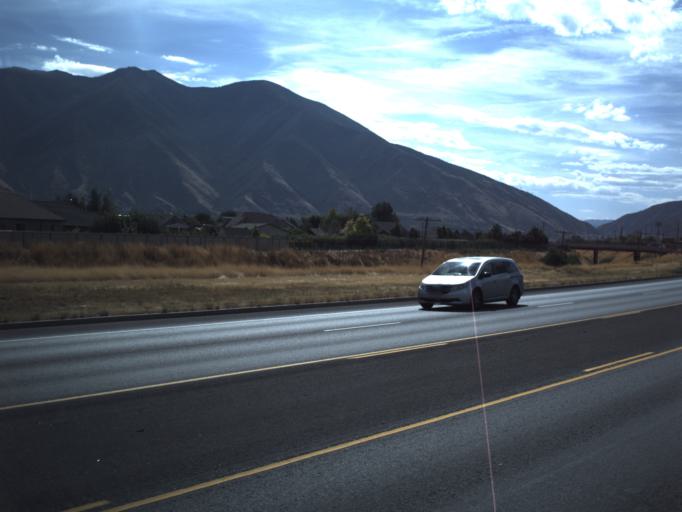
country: US
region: Utah
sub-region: Utah County
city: Spanish Fork
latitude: 40.1119
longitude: -111.6339
